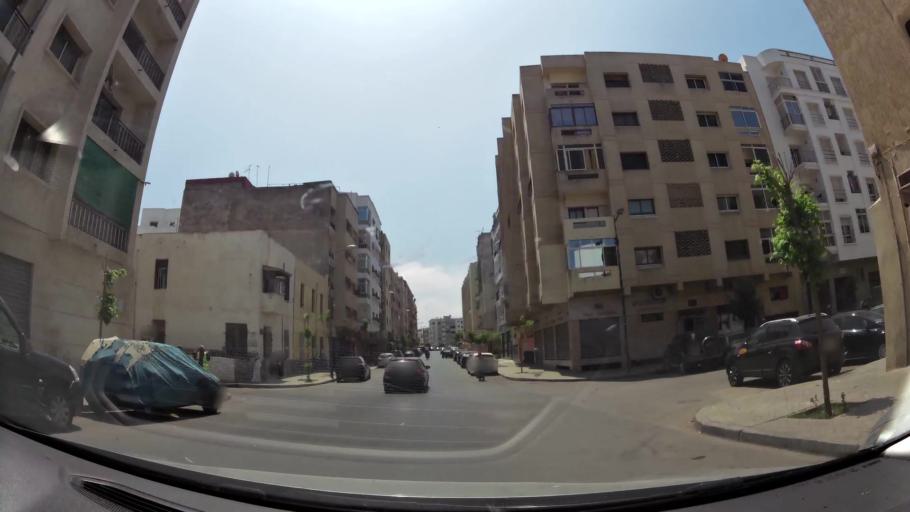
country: MA
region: Rabat-Sale-Zemmour-Zaer
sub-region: Rabat
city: Rabat
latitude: 34.0207
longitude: -6.8513
